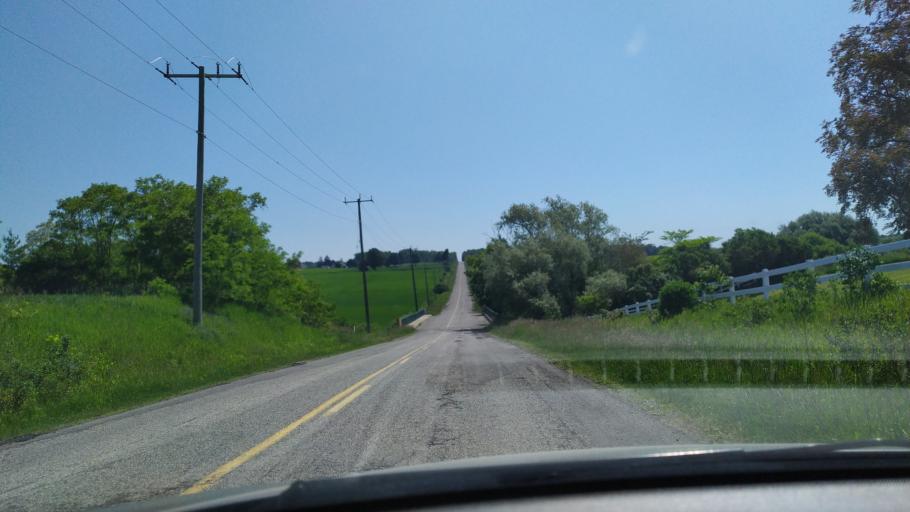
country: CA
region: Ontario
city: Waterloo
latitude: 43.4556
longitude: -80.7404
